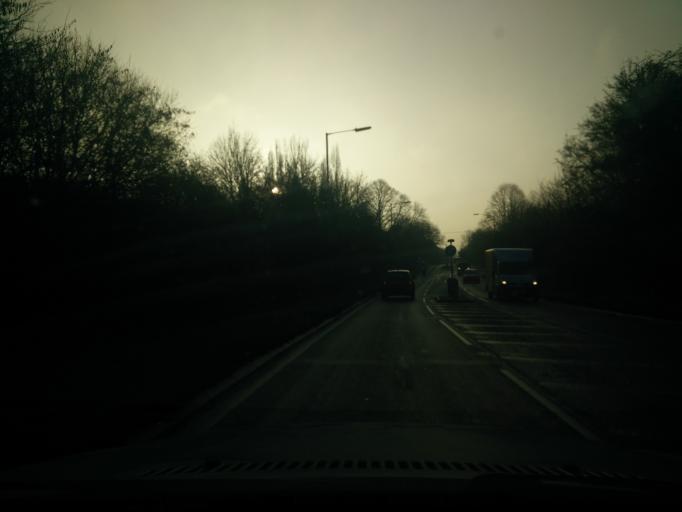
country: GB
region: England
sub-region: Buckinghamshire
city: Little Chalfont
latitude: 51.6553
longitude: -0.5845
